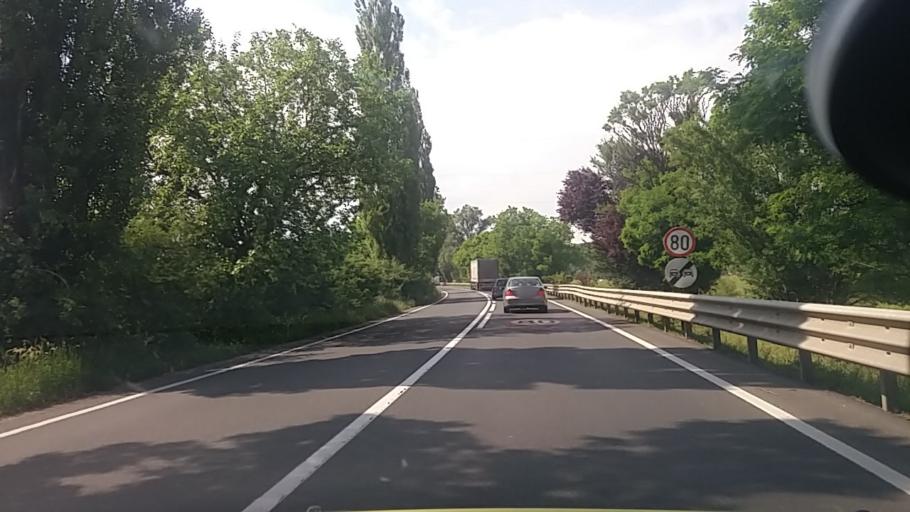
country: RO
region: Arad
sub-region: Comuna Varadia de Mures
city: Varadia de Mures
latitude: 46.0186
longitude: 22.1489
